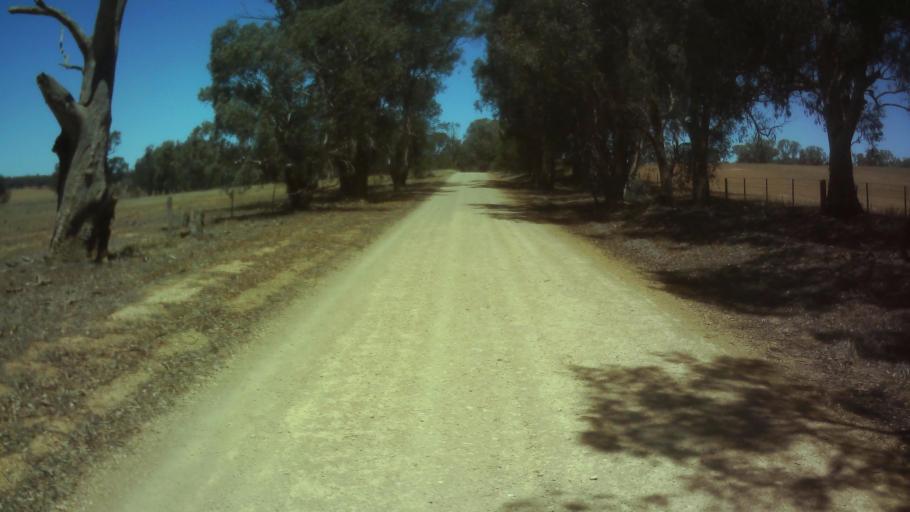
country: AU
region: New South Wales
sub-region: Weddin
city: Grenfell
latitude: -33.9116
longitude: 148.2141
